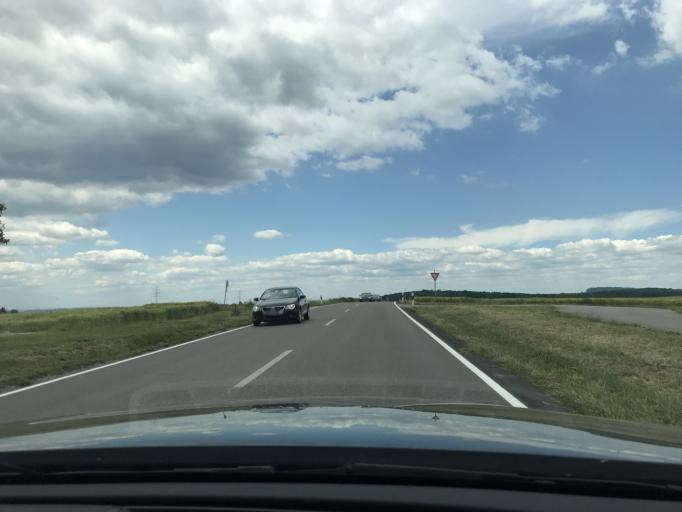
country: DE
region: Baden-Wuerttemberg
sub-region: Regierungsbezirk Stuttgart
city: Leutenbach
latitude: 48.8881
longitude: 9.3729
